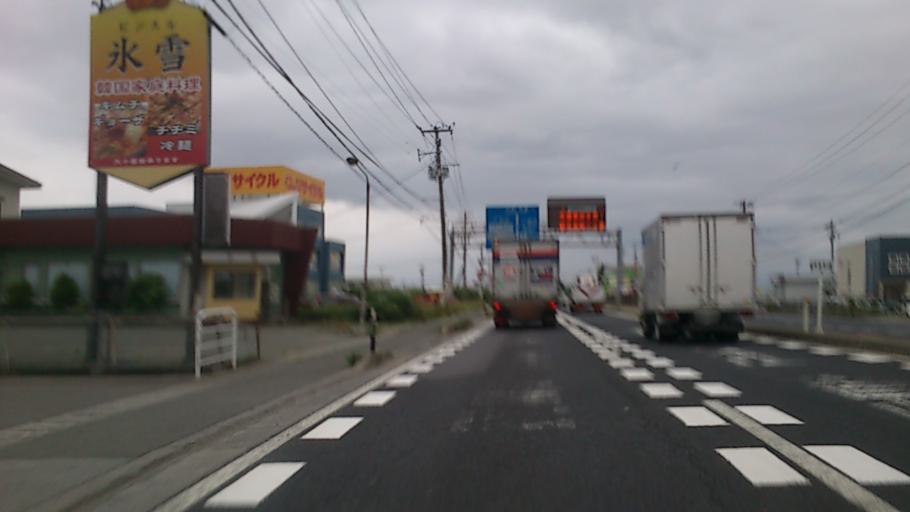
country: JP
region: Yamagata
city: Higashine
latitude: 38.4293
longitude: 140.3772
